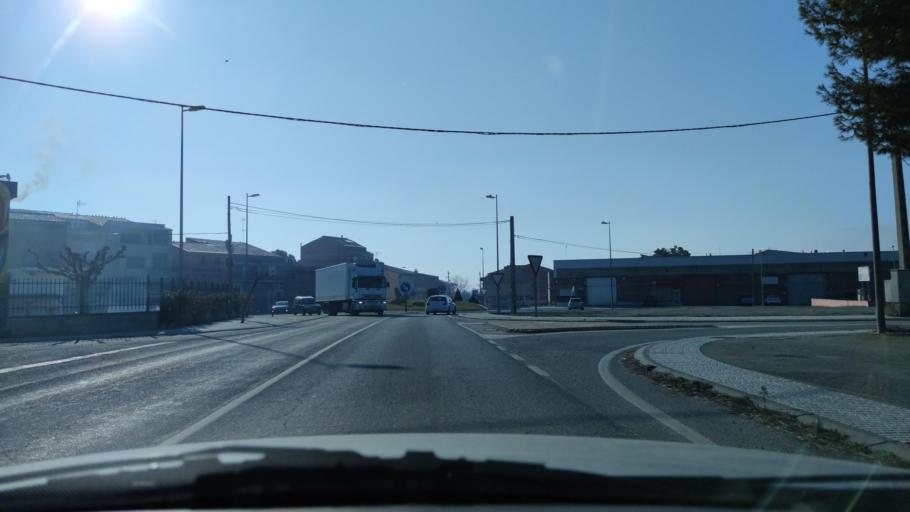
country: ES
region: Catalonia
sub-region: Provincia de Lleida
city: Torrefarrera
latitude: 41.6725
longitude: 0.6293
